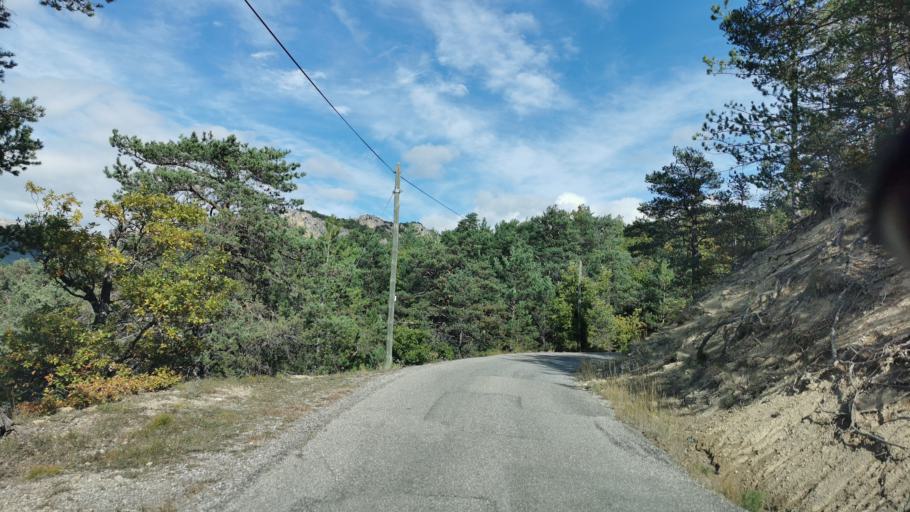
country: FR
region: Provence-Alpes-Cote d'Azur
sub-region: Departement des Alpes-de-Haute-Provence
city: Volonne
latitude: 44.1815
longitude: 6.0292
